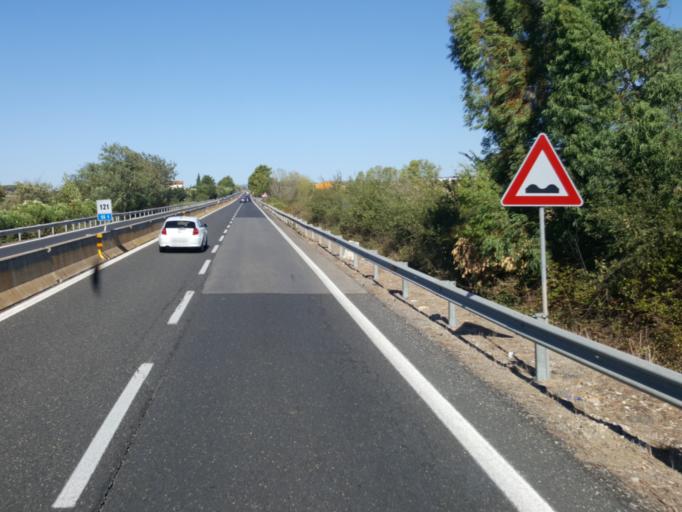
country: IT
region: Latium
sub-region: Provincia di Viterbo
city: Pescia Romana
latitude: 42.4035
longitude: 11.4958
